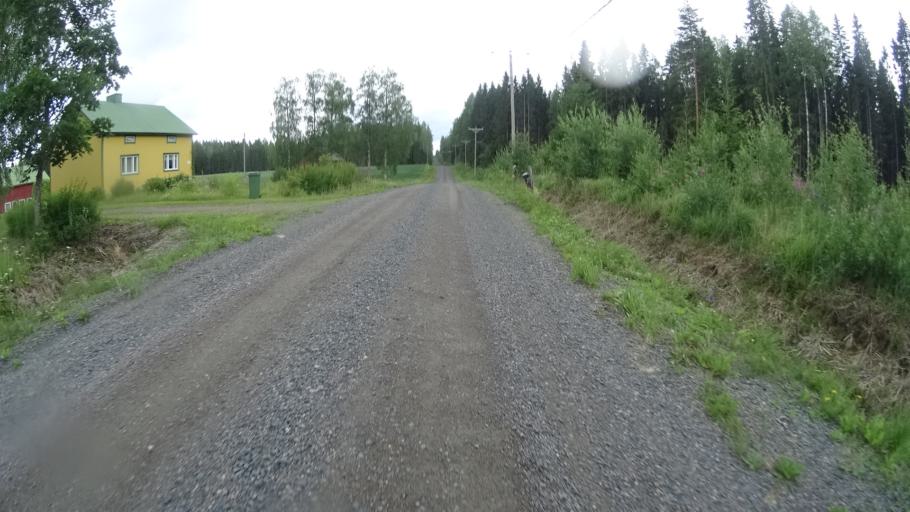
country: FI
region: Uusimaa
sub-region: Helsinki
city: Karkkila
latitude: 60.5914
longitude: 24.1599
